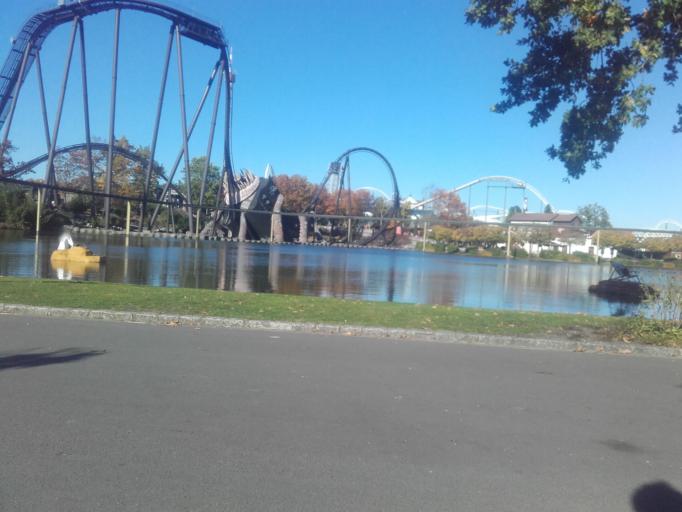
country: DE
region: Lower Saxony
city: Soltau
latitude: 53.0234
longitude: 9.8794
